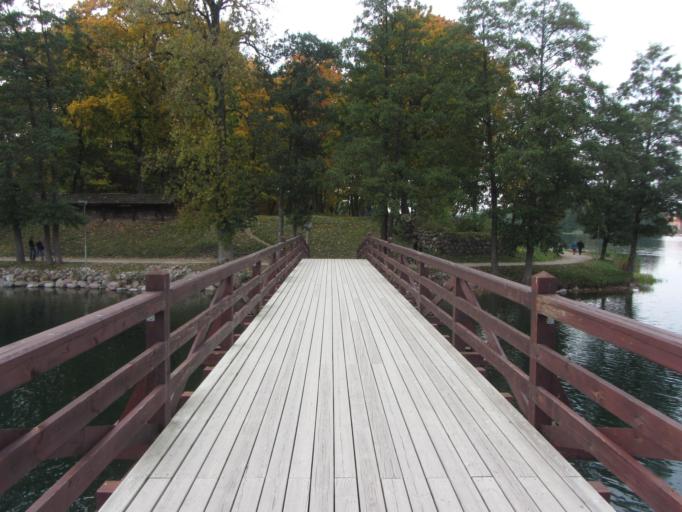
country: LT
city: Trakai
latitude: 54.6466
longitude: 24.9397
